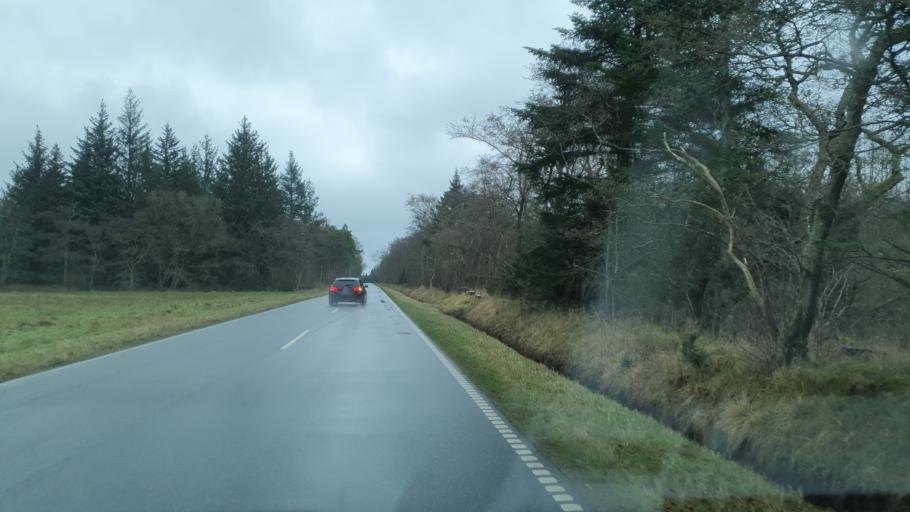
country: DK
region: North Denmark
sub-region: Jammerbugt Kommune
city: Fjerritslev
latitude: 57.1234
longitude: 9.1286
